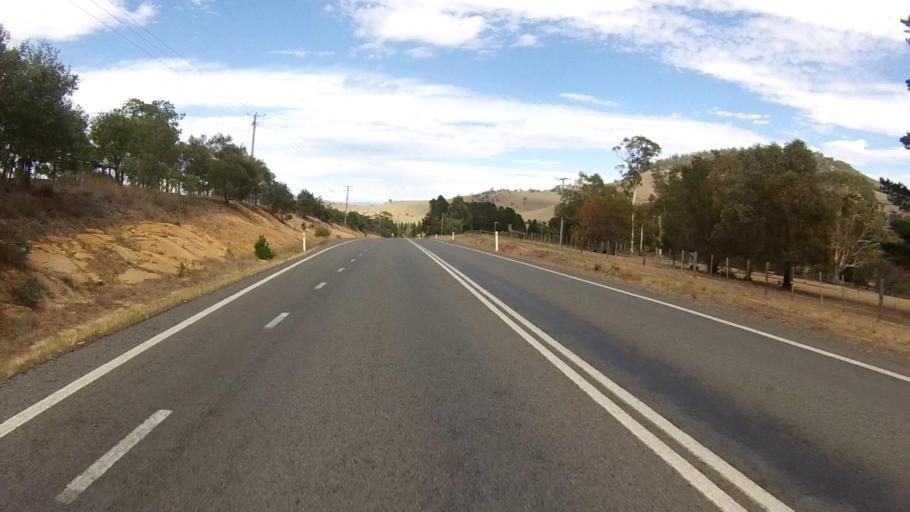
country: AU
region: Tasmania
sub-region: Brighton
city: Old Beach
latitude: -42.6699
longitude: 147.3674
